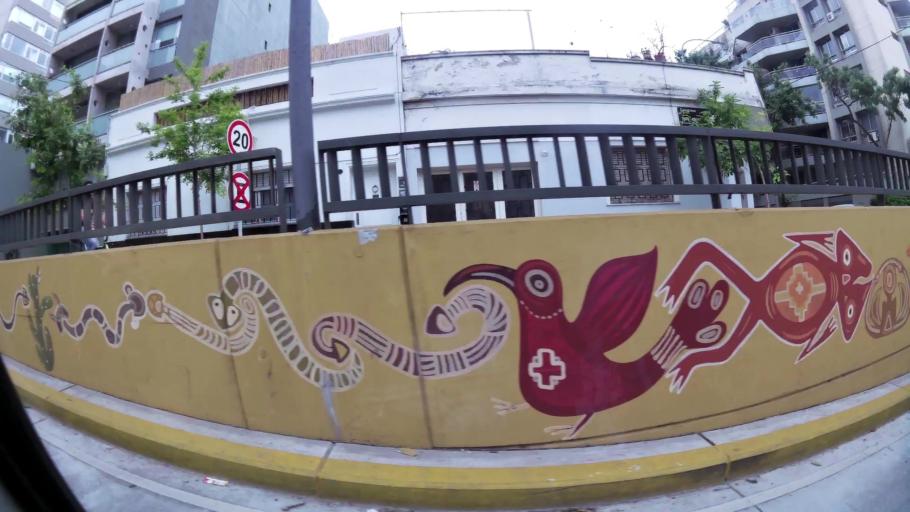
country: AR
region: Buenos Aires F.D.
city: Colegiales
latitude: -34.5530
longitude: -58.4575
